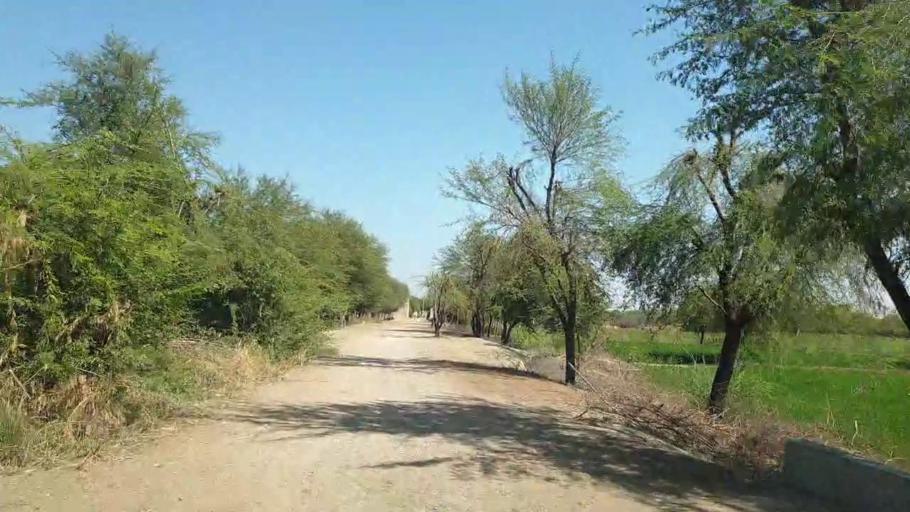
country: PK
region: Sindh
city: Mirpur Khas
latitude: 25.6170
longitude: 69.1336
